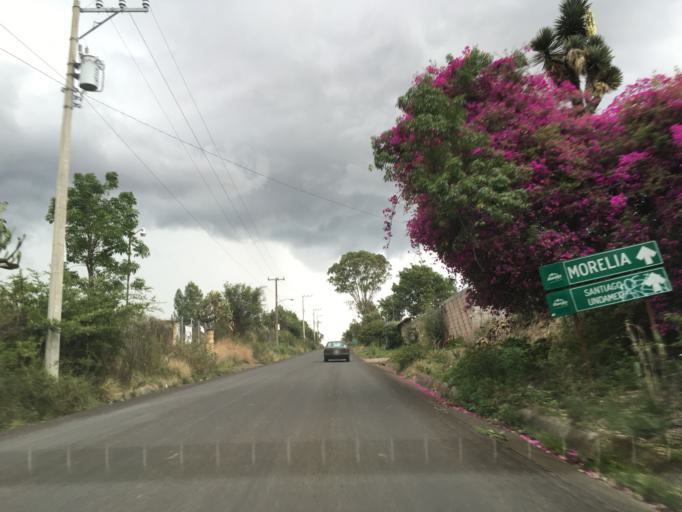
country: MX
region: Michoacan
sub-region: Morelia
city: La Mintzita (Piedra Dura)
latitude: 19.5924
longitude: -101.2738
